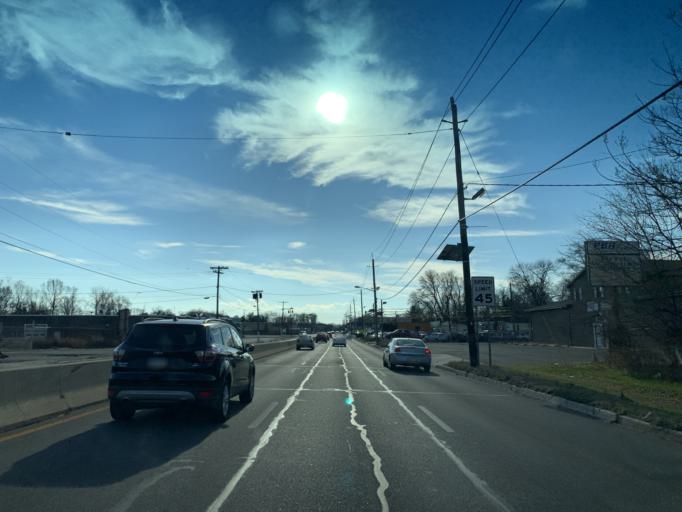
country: US
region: New Jersey
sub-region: Camden County
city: Audubon Park
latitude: 39.8984
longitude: -75.1003
